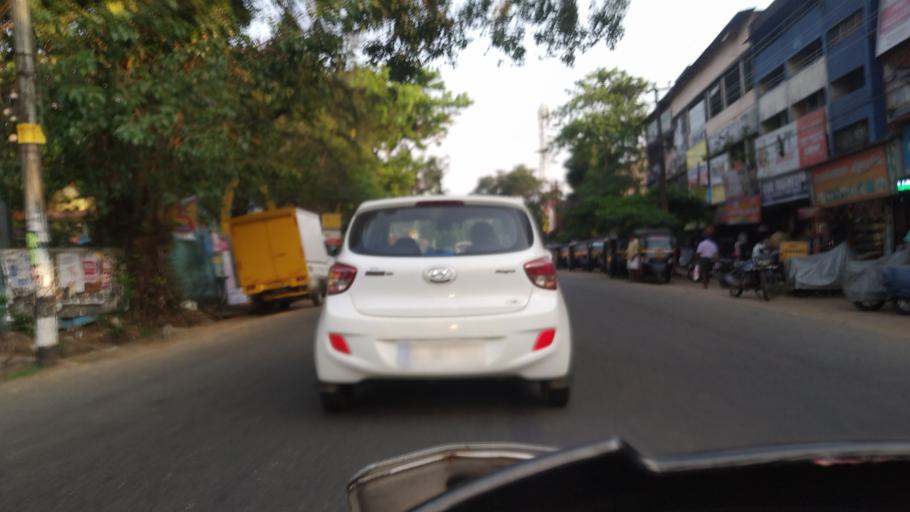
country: IN
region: Kerala
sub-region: Thrissur District
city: Irinjalakuda
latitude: 10.3151
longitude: 76.1472
